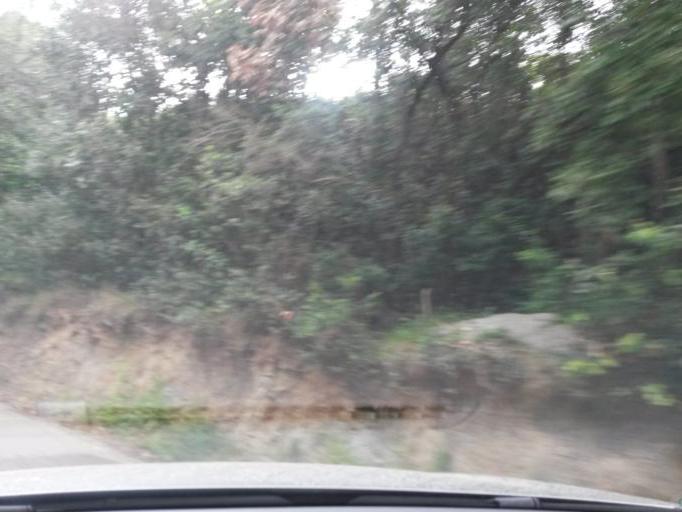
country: IT
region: Tuscany
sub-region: Provincia di Livorno
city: Capoliveri
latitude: 42.7548
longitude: 10.3626
